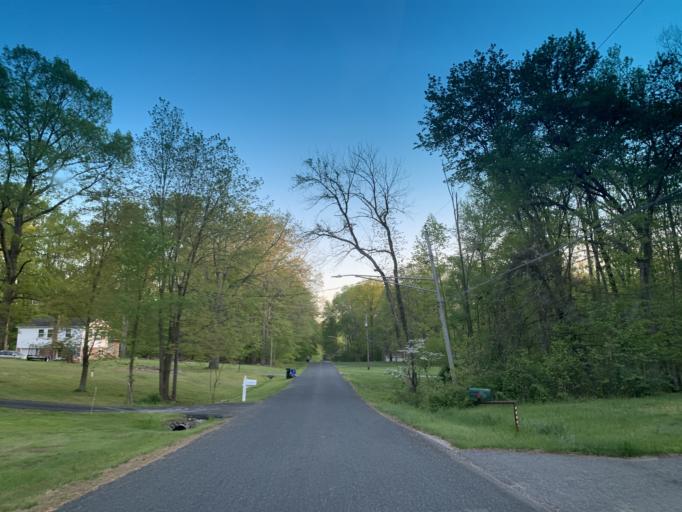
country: US
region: Maryland
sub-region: Harford County
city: Riverside
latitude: 39.5289
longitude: -76.2237
